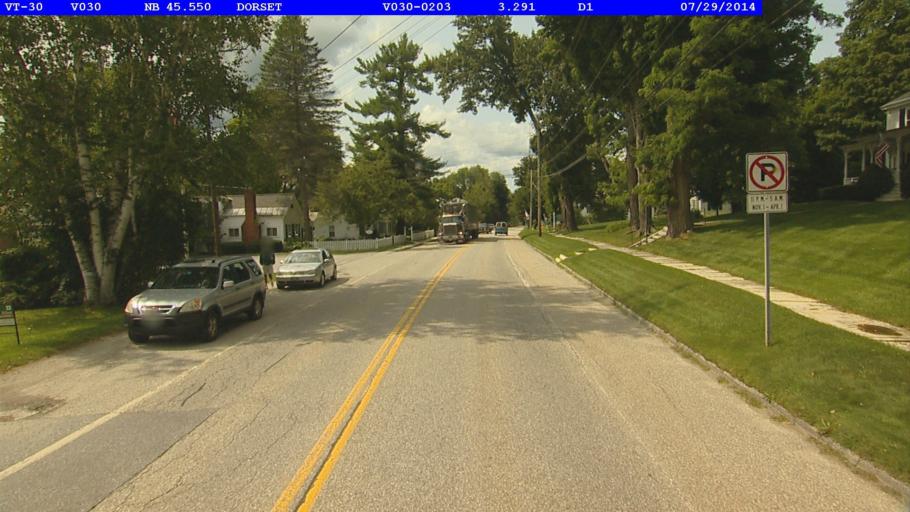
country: US
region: Vermont
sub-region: Bennington County
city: Manchester Center
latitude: 43.2539
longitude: -73.0979
